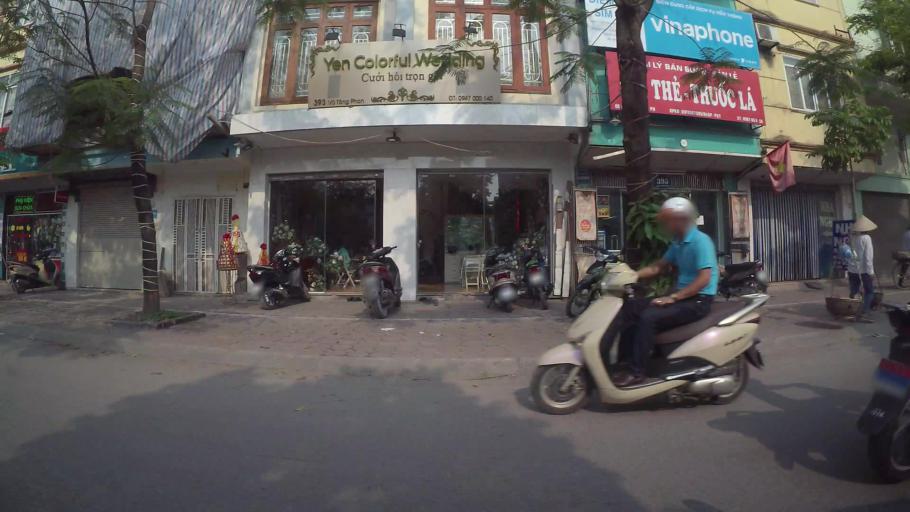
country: VN
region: Ha Noi
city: Thanh Xuan
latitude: 20.9892
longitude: 105.8136
